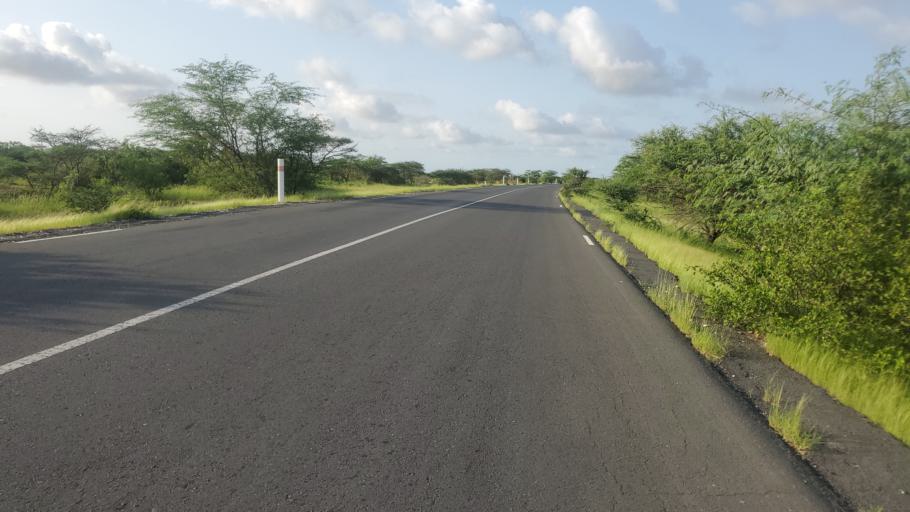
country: SN
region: Saint-Louis
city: Saint-Louis
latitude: 16.1194
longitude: -16.4142
